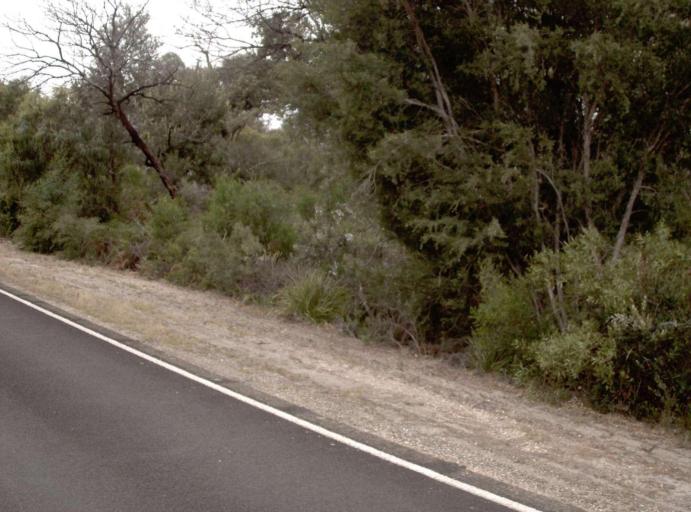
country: AU
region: Victoria
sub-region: East Gippsland
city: Bairnsdale
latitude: -38.0679
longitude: 147.5529
